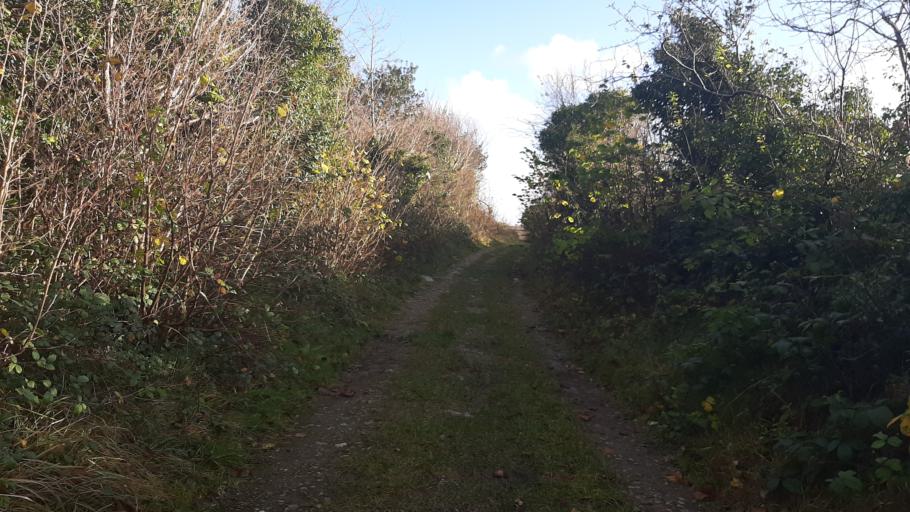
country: IE
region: Connaught
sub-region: County Galway
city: Gaillimh
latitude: 53.3020
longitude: -9.0604
